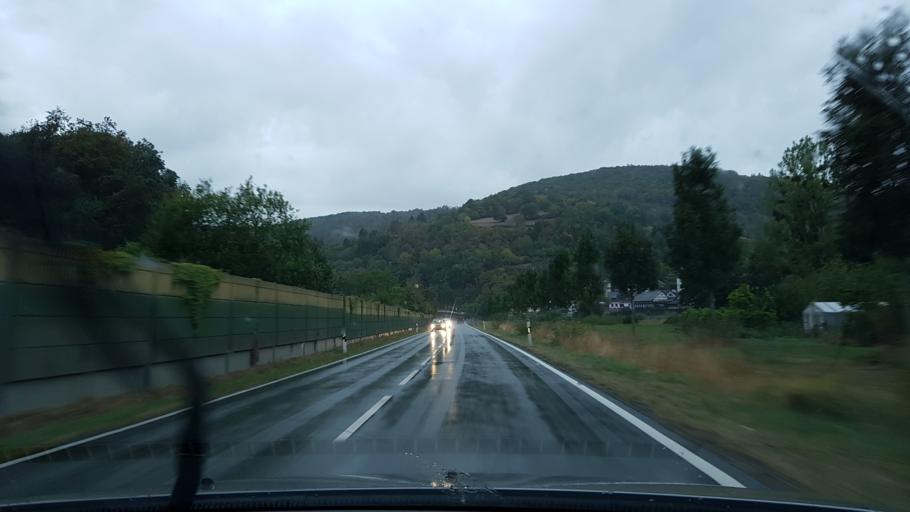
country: DE
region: Rheinland-Pfalz
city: Dausenau
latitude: 50.3258
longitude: 7.7628
